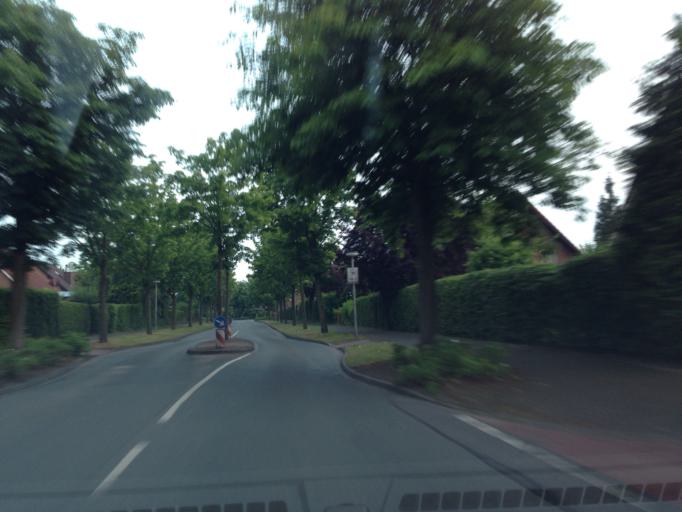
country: DE
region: North Rhine-Westphalia
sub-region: Regierungsbezirk Munster
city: Senden
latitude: 51.8651
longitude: 7.4808
